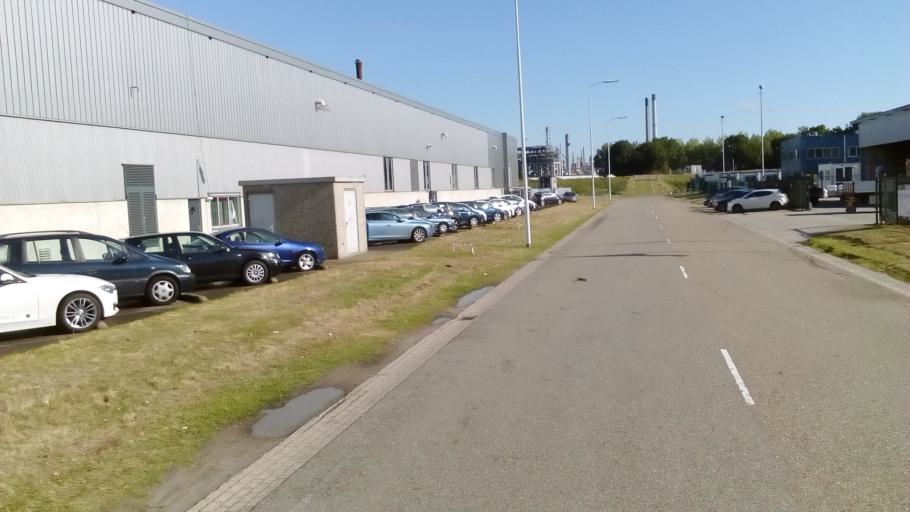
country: NL
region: North Brabant
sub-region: Gemeente Moerdijk
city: Klundert
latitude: 51.6763
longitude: 4.5470
